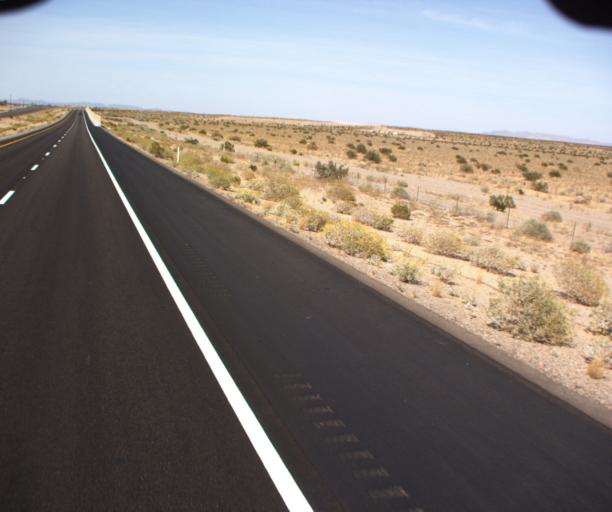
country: US
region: Arizona
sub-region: Yuma County
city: Somerton
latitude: 32.5467
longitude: -114.5620
